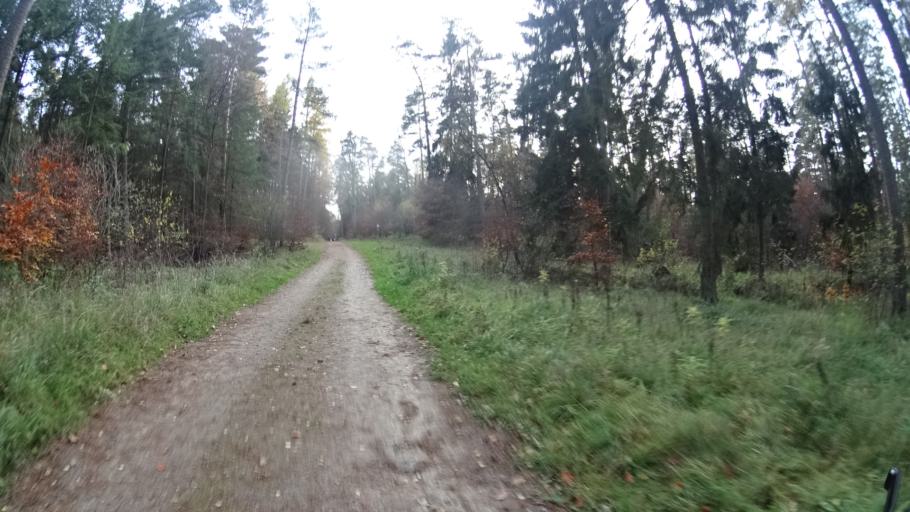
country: DE
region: Lower Saxony
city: Deutsch Evern
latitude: 53.2225
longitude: 10.4310
